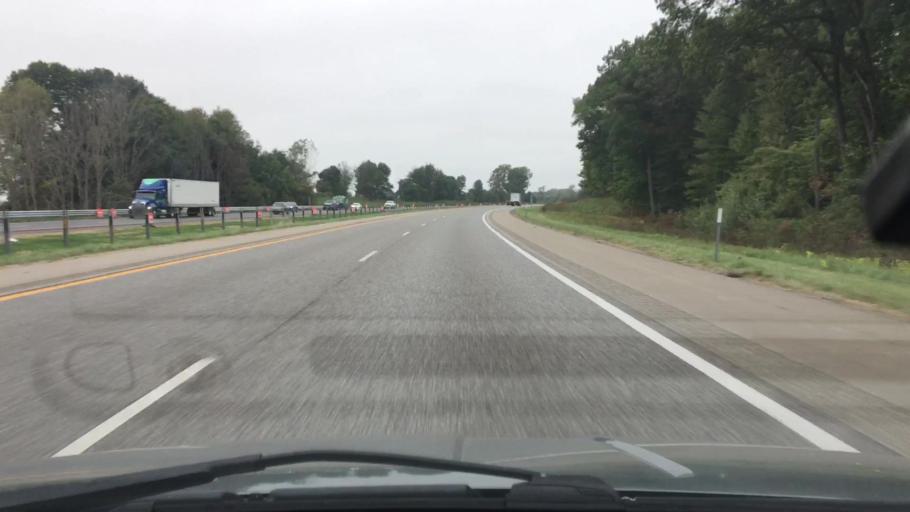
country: US
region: Michigan
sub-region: Van Buren County
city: Decatur
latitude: 42.1902
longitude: -85.9989
